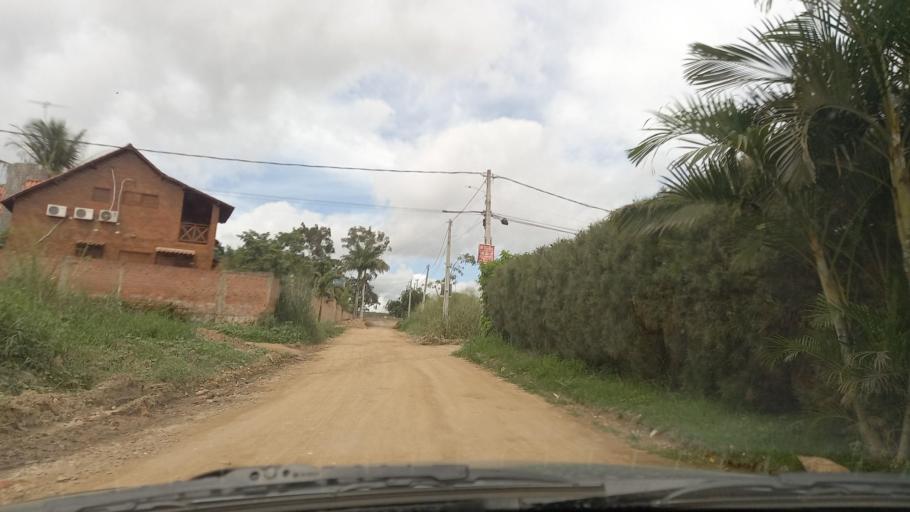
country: BR
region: Pernambuco
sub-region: Gravata
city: Gravata
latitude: -8.1967
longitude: -35.5854
